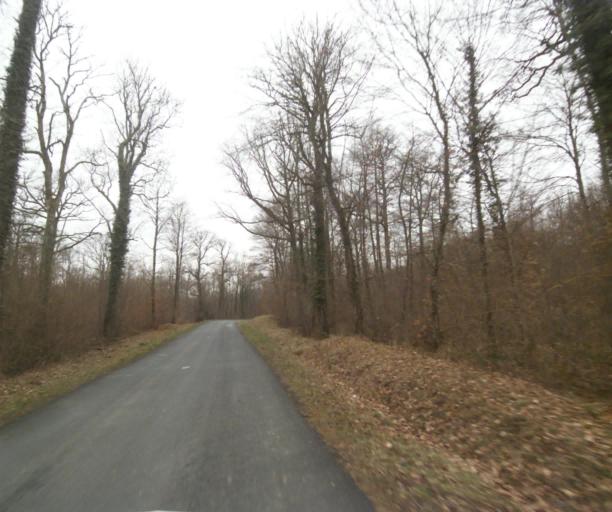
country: FR
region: Champagne-Ardenne
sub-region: Departement de la Haute-Marne
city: Bienville
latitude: 48.5651
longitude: 5.0153
